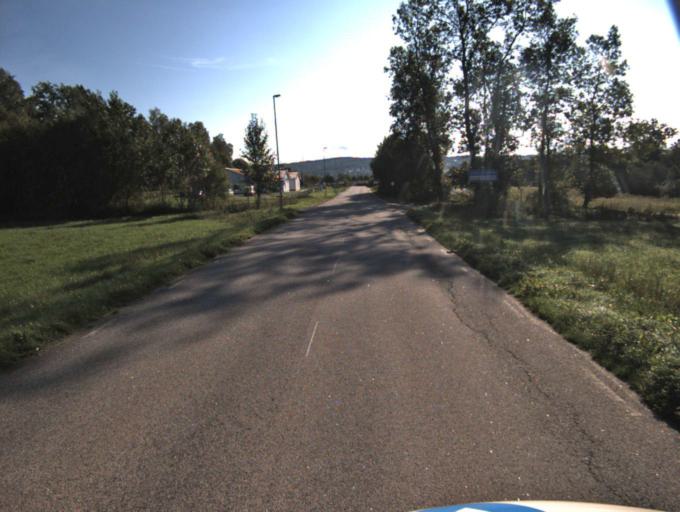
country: SE
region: Vaestra Goetaland
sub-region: Ulricehamns Kommun
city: Ulricehamn
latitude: 57.7987
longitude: 13.3876
